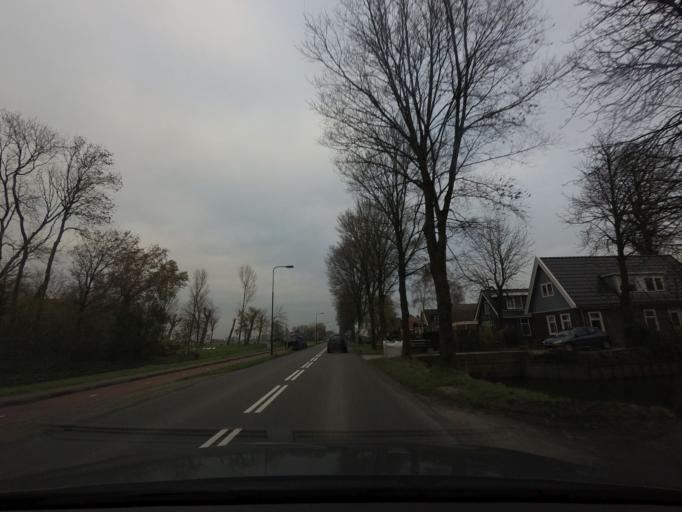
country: NL
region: North Holland
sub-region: Gemeente Heerhugowaard
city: Heerhugowaard
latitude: 52.6853
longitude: 4.8499
